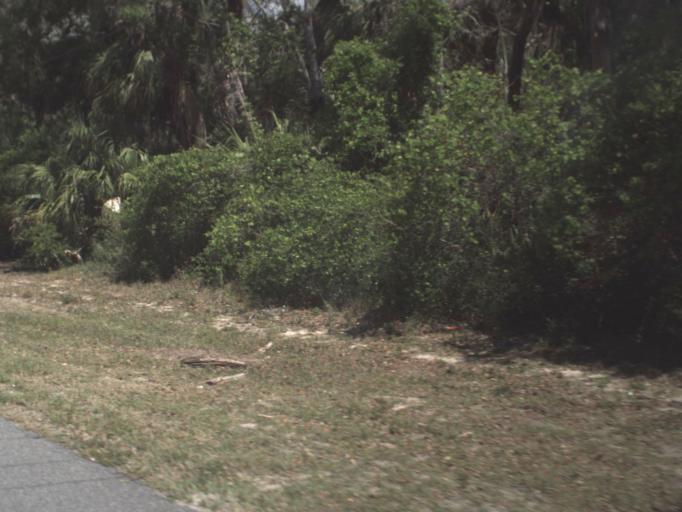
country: US
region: Florida
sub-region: Flagler County
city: Palm Coast
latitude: 29.6124
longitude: -81.2017
